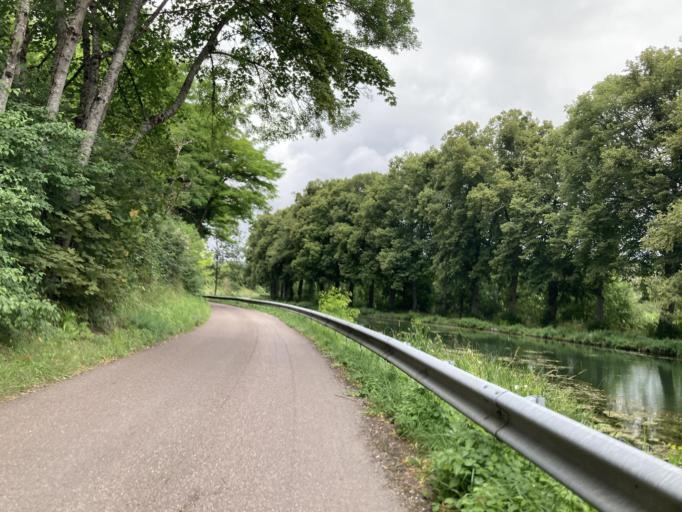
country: FR
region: Bourgogne
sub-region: Departement de la Cote-d'Or
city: Plombieres-les-Dijon
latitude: 47.3303
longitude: 4.9824
